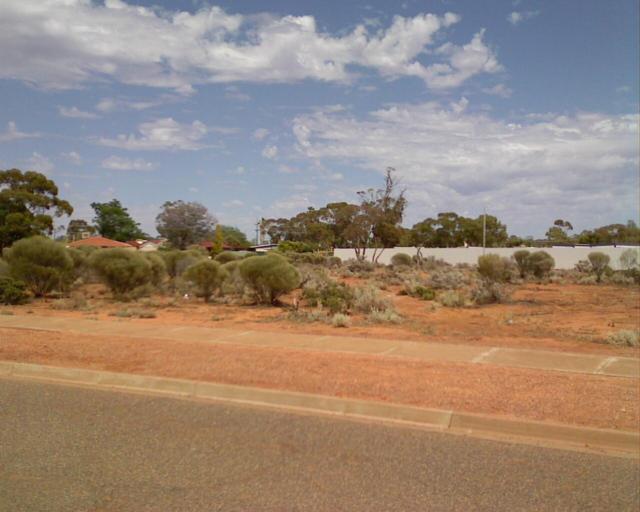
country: AU
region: Western Australia
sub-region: Kalgoorlie/Boulder
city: Stoneville
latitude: -31.2097
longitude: 121.6199
